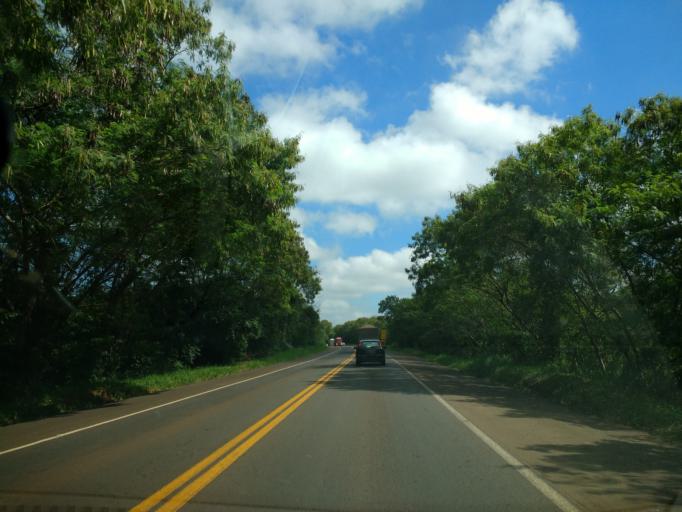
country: BR
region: Parana
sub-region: Cruzeiro Do Oeste
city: Cruzeiro do Oeste
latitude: -23.7648
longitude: -53.1392
